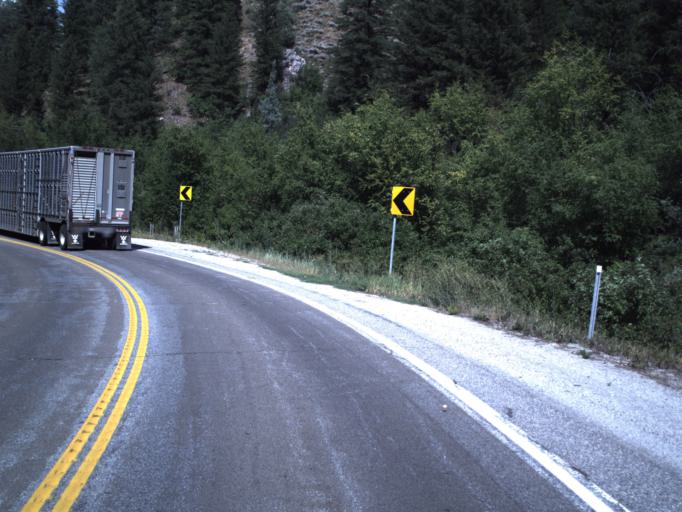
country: US
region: Utah
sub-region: Cache County
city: North Logan
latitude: 41.8139
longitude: -111.6190
